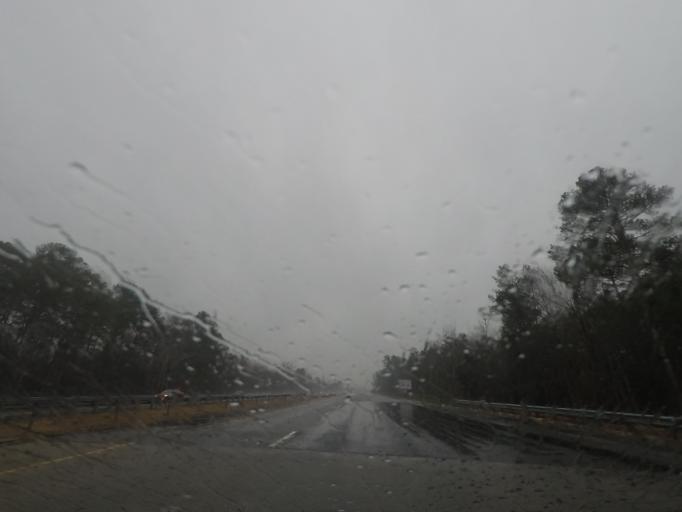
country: US
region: North Carolina
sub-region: Wake County
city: Morrisville
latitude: 35.8913
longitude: -78.8736
